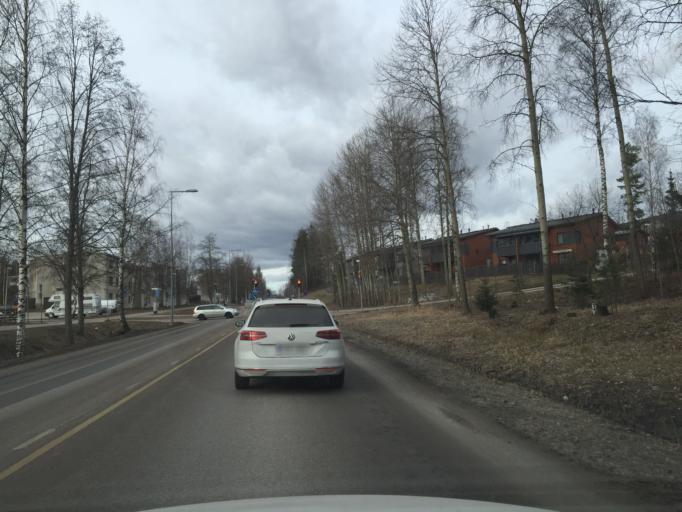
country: FI
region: Uusimaa
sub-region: Helsinki
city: Teekkarikylae
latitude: 60.2818
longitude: 24.8728
